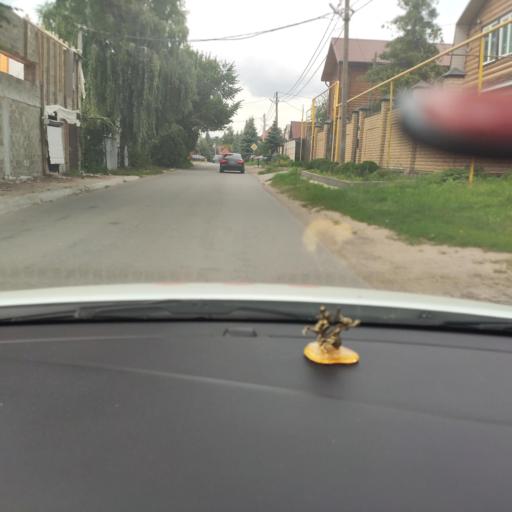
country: RU
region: Tatarstan
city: Verkhniy Uslon
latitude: 55.6164
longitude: 49.0164
